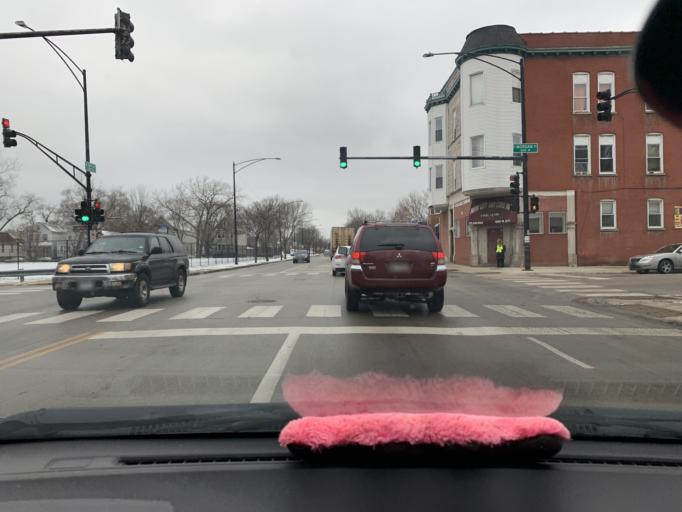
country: US
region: Illinois
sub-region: Cook County
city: Chicago
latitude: 41.8015
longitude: -87.6500
